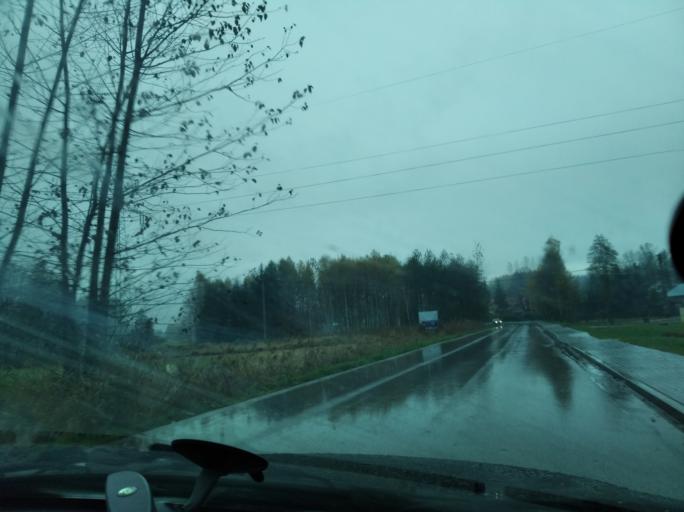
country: PL
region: Subcarpathian Voivodeship
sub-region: Powiat lancucki
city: Albigowa
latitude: 50.0376
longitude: 22.2059
